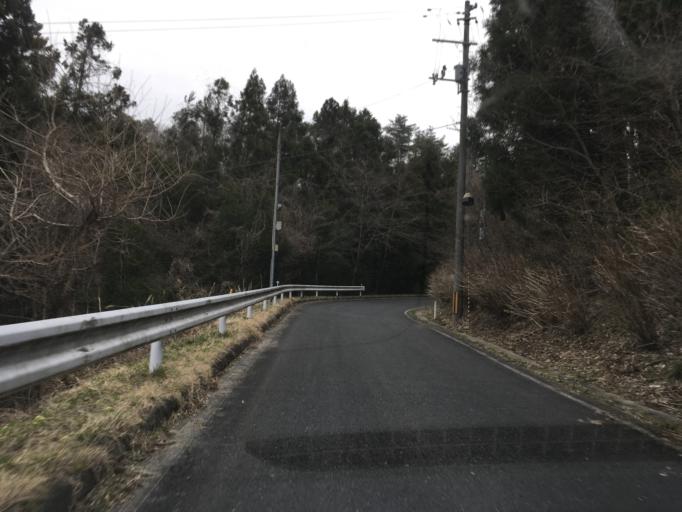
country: JP
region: Iwate
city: Ichinoseki
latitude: 38.7604
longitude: 141.2234
